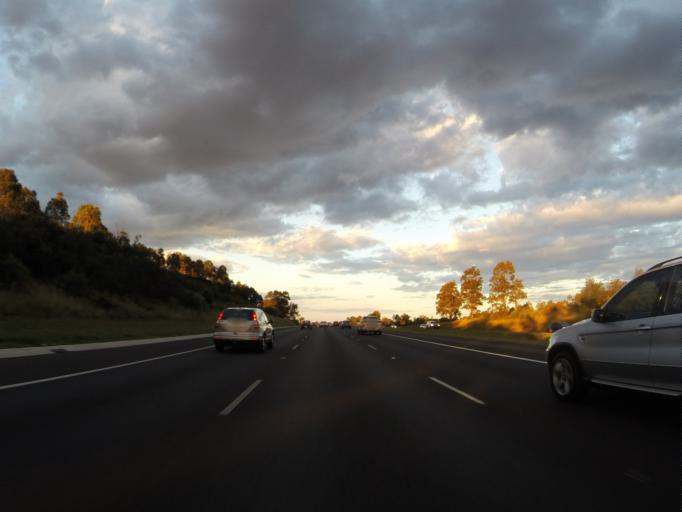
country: AU
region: New South Wales
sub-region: Campbelltown Municipality
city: Campbelltown
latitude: -34.0536
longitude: 150.8062
